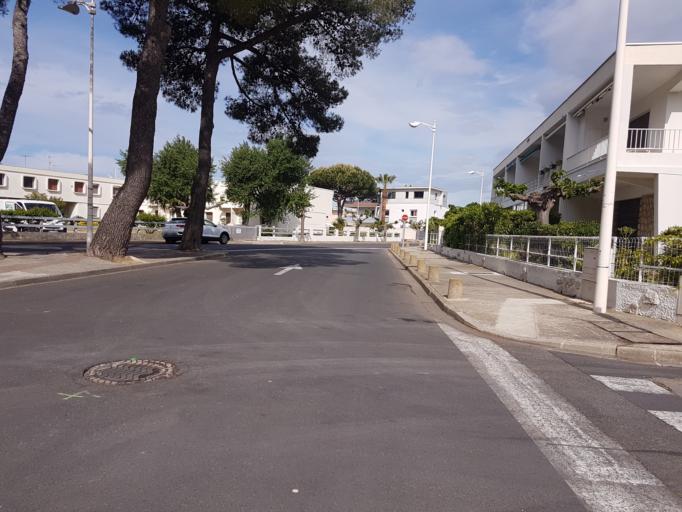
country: FR
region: Languedoc-Roussillon
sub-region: Departement du Gard
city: Le Grau-du-Roi
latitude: 43.5440
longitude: 4.1304
